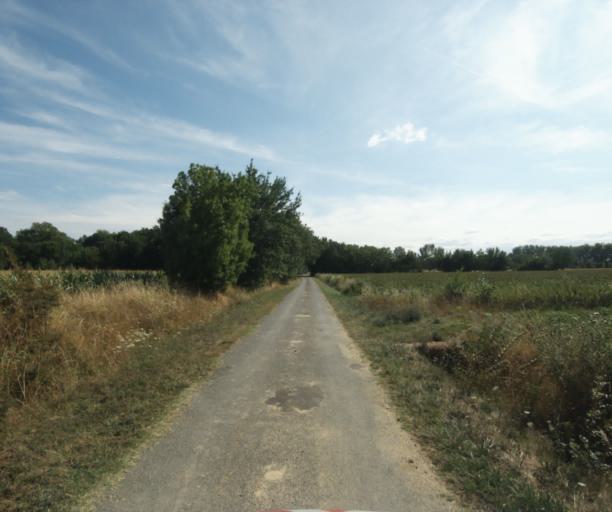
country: FR
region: Midi-Pyrenees
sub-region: Departement de la Haute-Garonne
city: Revel
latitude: 43.5002
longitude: 1.9671
